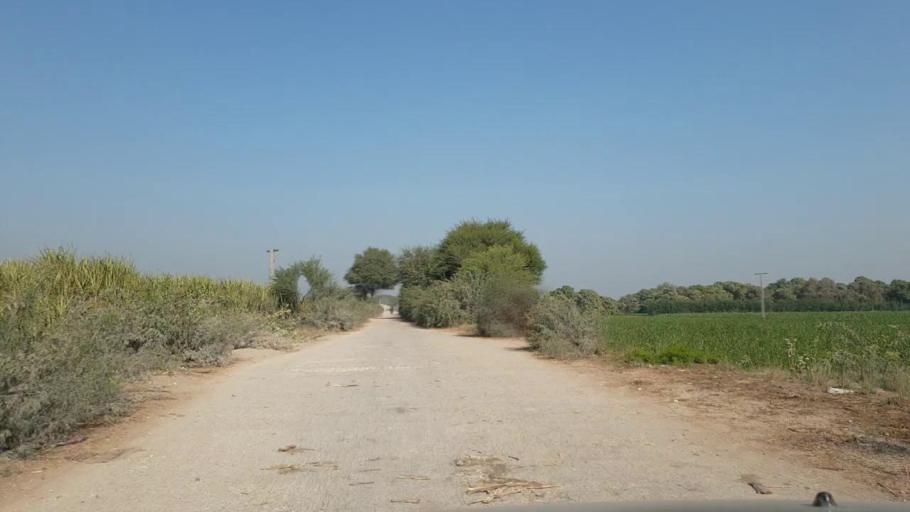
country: PK
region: Sindh
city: Tando Allahyar
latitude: 25.5673
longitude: 68.6080
